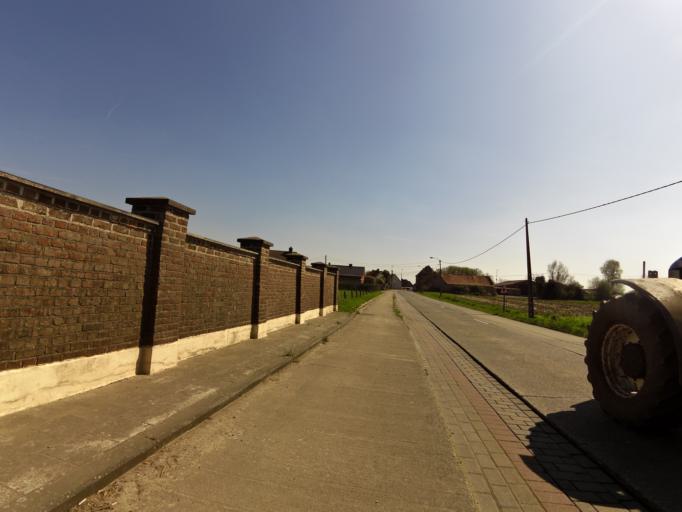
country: BE
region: Flanders
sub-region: Provincie West-Vlaanderen
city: Kortemark
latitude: 51.0474
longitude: 3.0347
